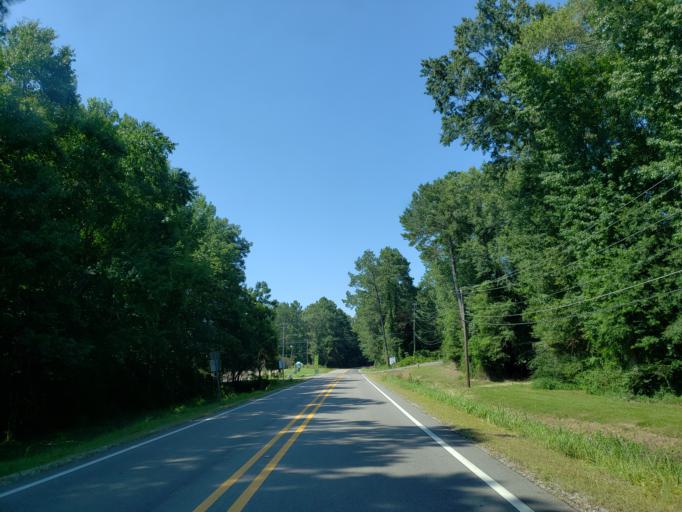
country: US
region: Mississippi
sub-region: Lamar County
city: Sumrall
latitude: 31.4218
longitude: -89.5459
